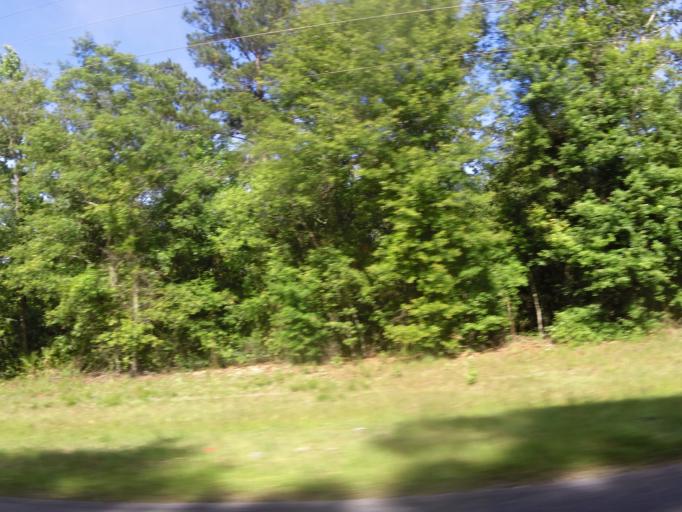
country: US
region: Florida
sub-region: Nassau County
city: Hilliard
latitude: 30.6738
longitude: -81.9046
